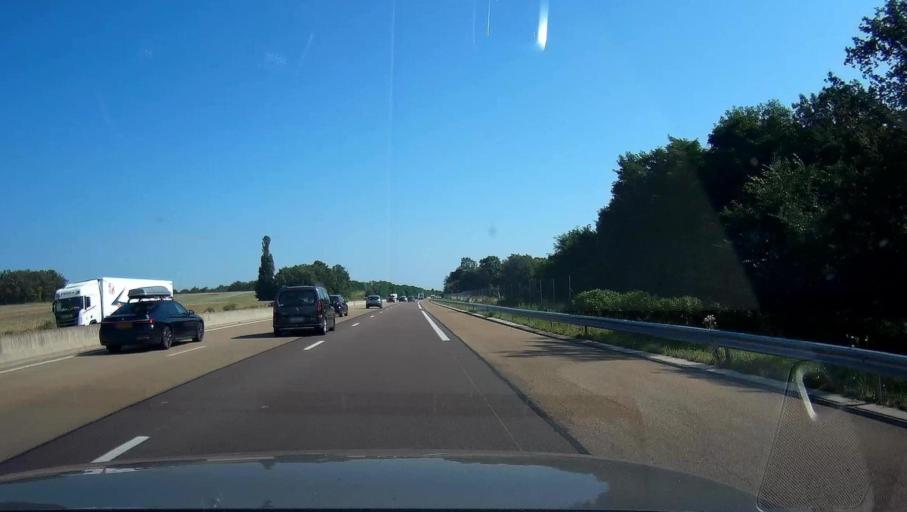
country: FR
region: Bourgogne
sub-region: Departement de la Cote-d'Or
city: Saint-Julien
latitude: 47.4586
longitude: 5.1764
